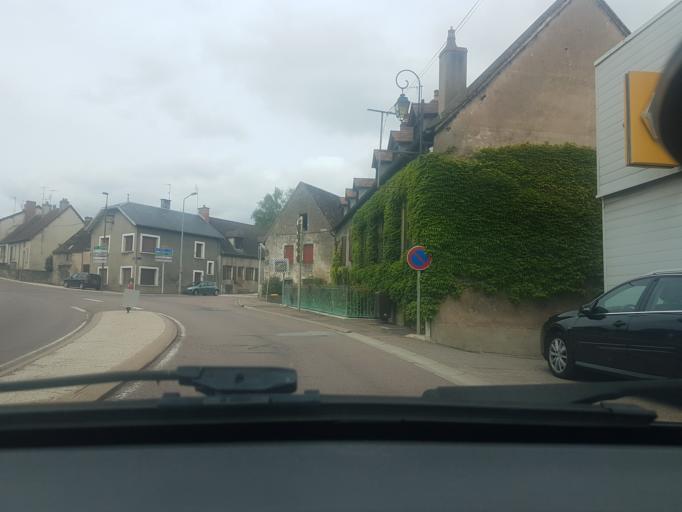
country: FR
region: Bourgogne
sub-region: Departement de la Cote-d'Or
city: Arnay-le-Duc
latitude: 47.1361
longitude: 4.4854
